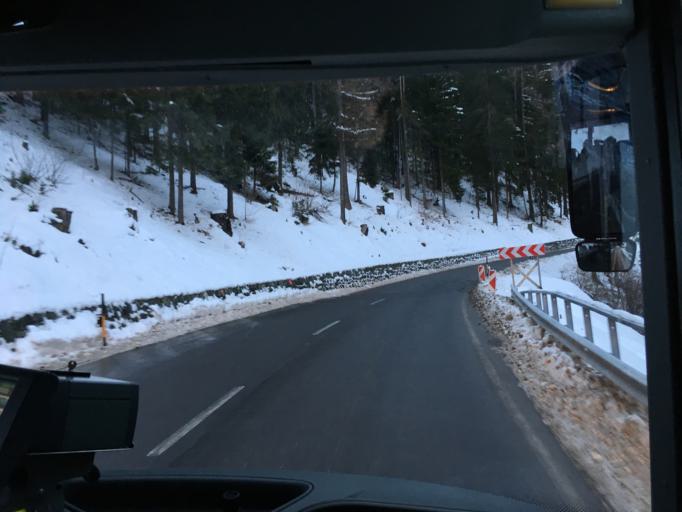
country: CH
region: Grisons
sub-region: Albula District
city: Tiefencastel
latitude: 46.5715
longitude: 9.6239
